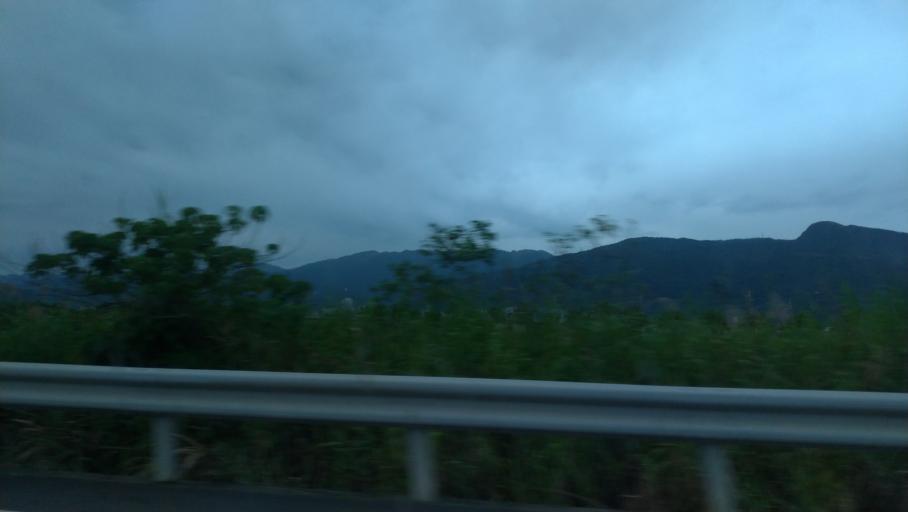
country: TW
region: Taiwan
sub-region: Yilan
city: Yilan
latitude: 24.8213
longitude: 121.7977
